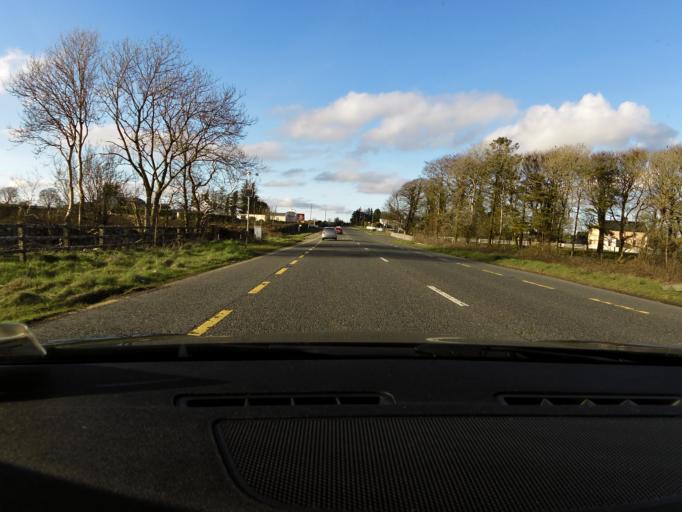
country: IE
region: Connaught
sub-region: Roscommon
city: Roscommon
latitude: 53.6759
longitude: -8.1975
